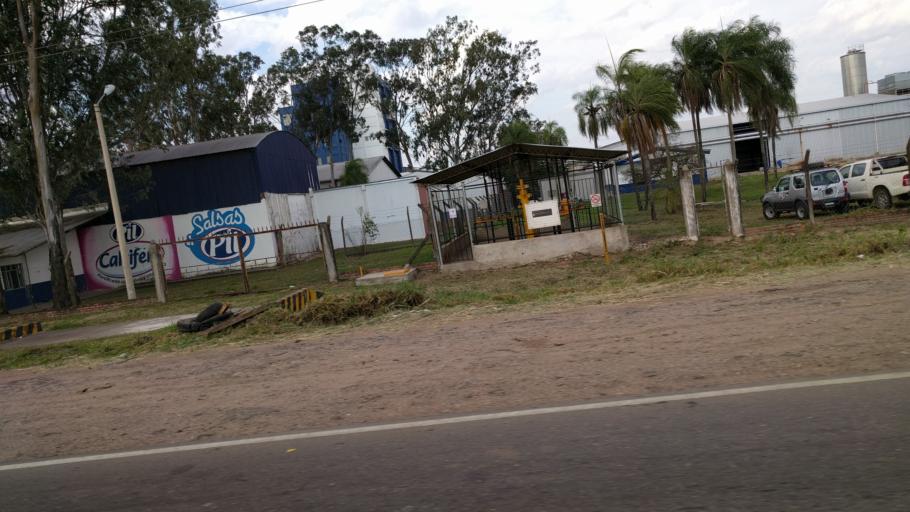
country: BO
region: Santa Cruz
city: Warnes
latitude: -17.5325
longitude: -63.1613
